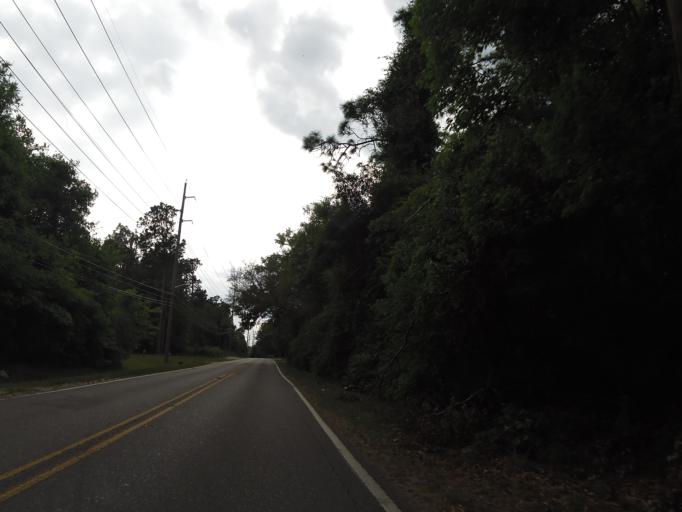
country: US
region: Florida
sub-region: Clay County
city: Bellair-Meadowbrook Terrace
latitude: 30.1964
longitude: -81.7184
